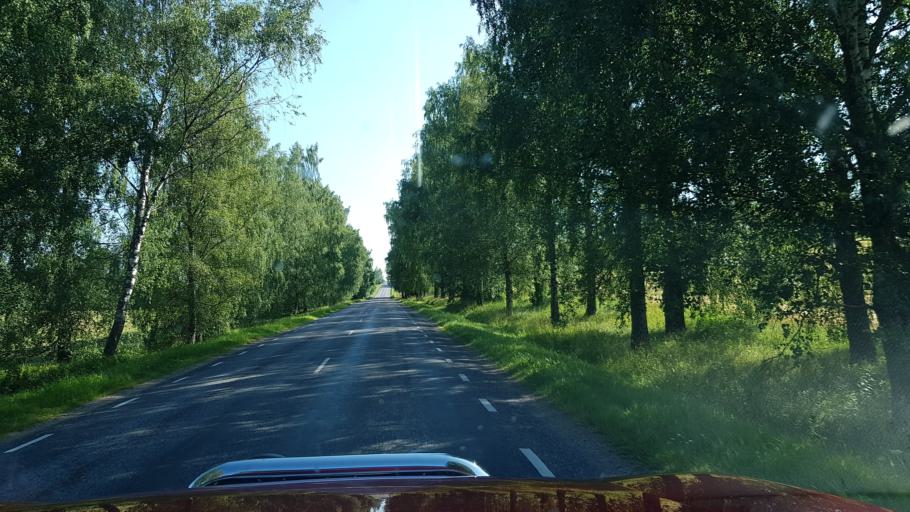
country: EE
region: Polvamaa
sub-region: Polva linn
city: Polva
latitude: 57.9837
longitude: 26.8800
